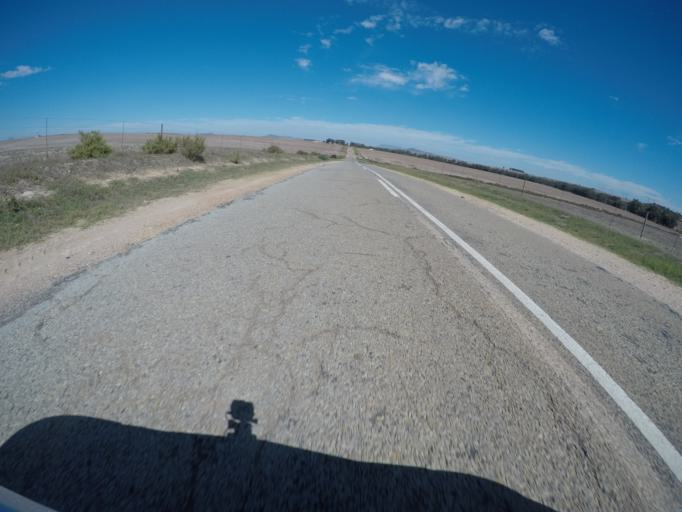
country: ZA
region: Western Cape
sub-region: City of Cape Town
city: Atlantis
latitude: -33.6015
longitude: 18.6412
